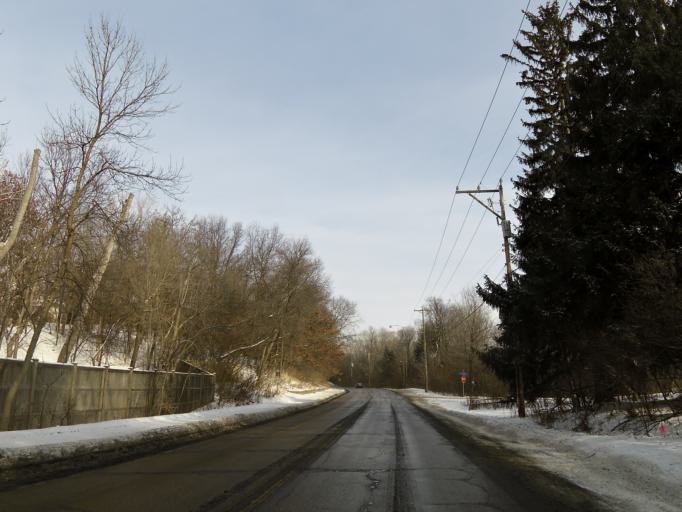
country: US
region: Minnesota
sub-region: Hennepin County
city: Minnetonka
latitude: 44.9045
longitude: -93.5070
